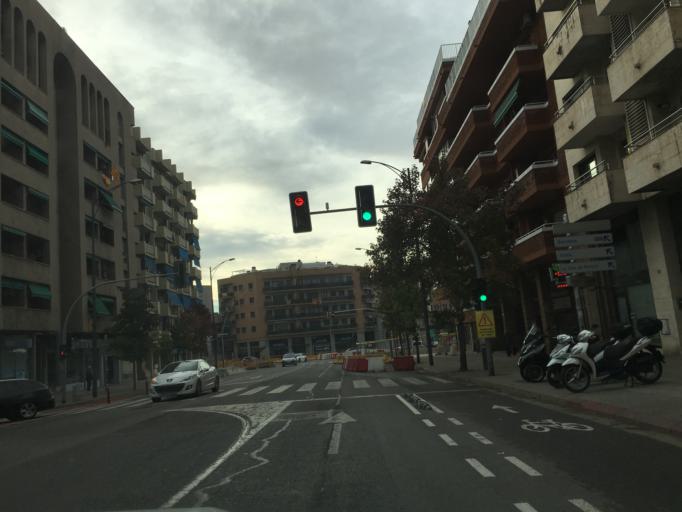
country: ES
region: Catalonia
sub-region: Provincia de Barcelona
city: Sabadell
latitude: 41.5453
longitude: 2.0997
